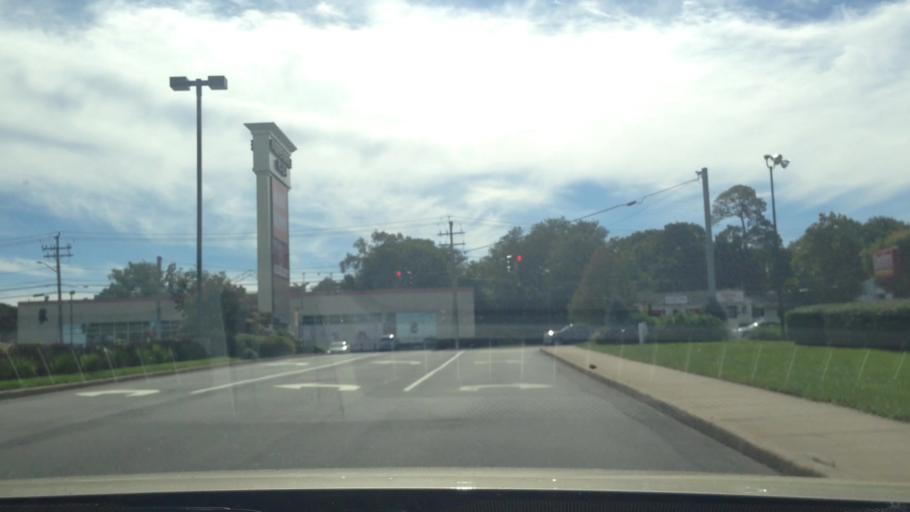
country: US
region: New York
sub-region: Suffolk County
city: Selden
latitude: 40.8639
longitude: -73.0521
